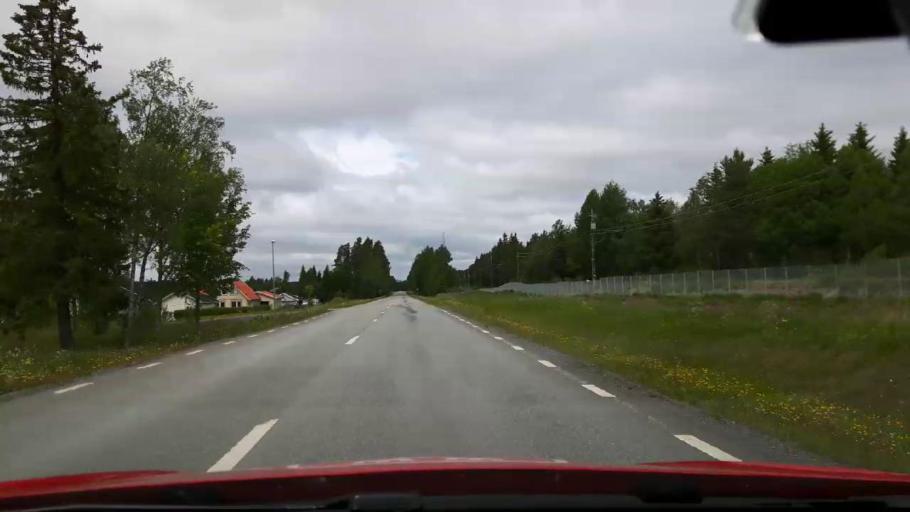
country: SE
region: Jaemtland
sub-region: Krokoms Kommun
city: Krokom
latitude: 63.2921
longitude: 14.4921
